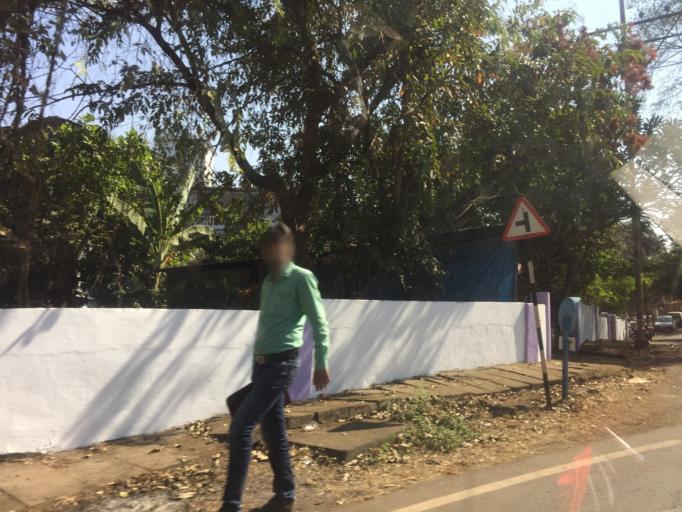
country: IN
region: Goa
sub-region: South Goa
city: Vasco Da Gama
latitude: 15.3934
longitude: 73.8182
